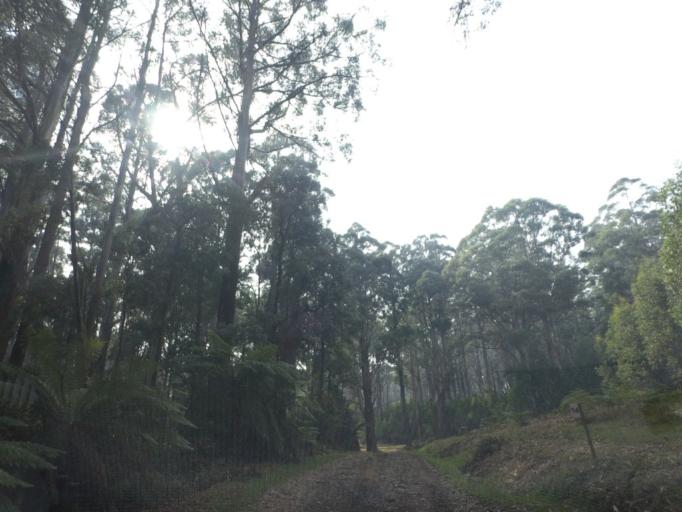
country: AU
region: Victoria
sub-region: Yarra Ranges
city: Healesville
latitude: -37.5672
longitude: 145.5858
